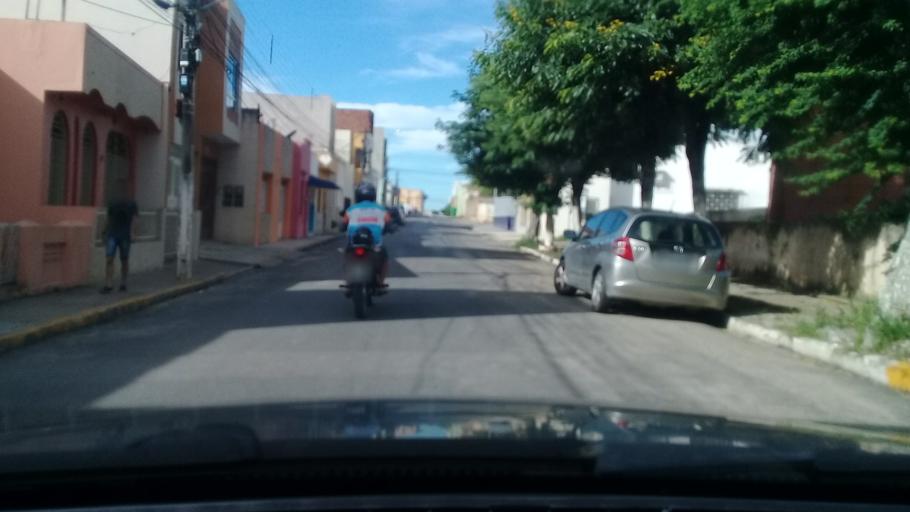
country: BR
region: Pernambuco
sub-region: Vitoria De Santo Antao
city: Vitoria de Santo Antao
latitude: -8.1142
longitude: -35.2922
